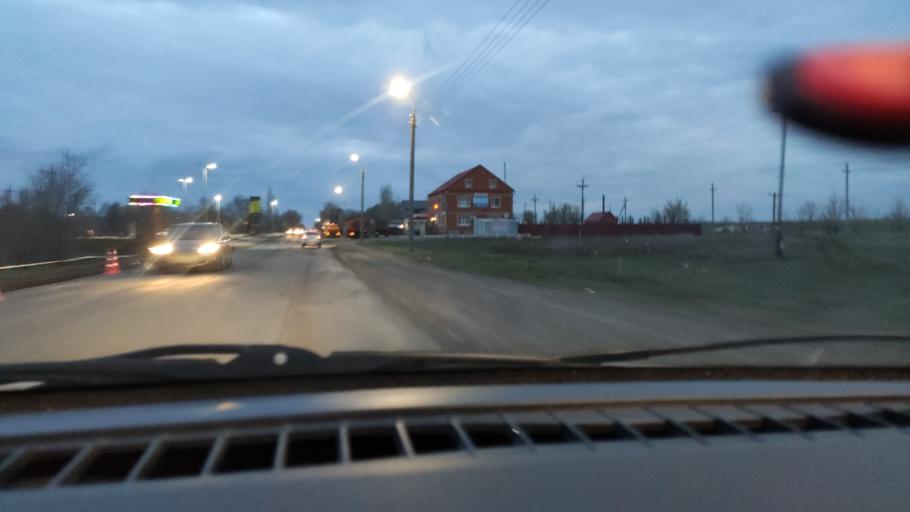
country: RU
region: Orenburg
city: Tatarskaya Kargala
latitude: 51.8695
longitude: 55.1434
